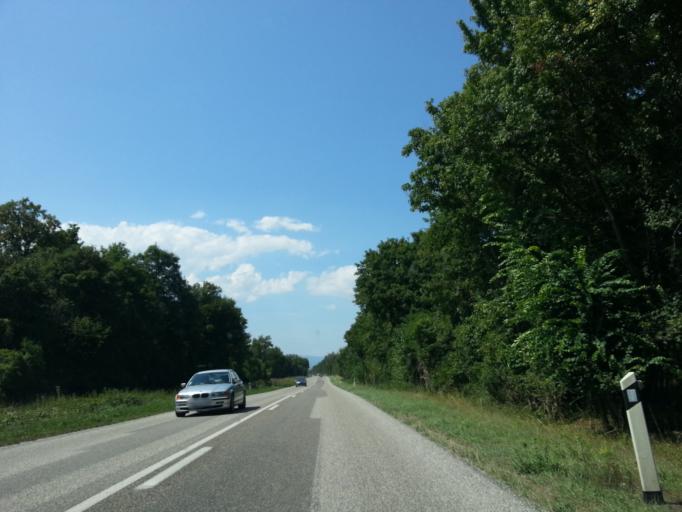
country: FR
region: Alsace
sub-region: Departement du Haut-Rhin
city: Wolfgantzen
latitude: 48.0386
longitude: 7.4796
